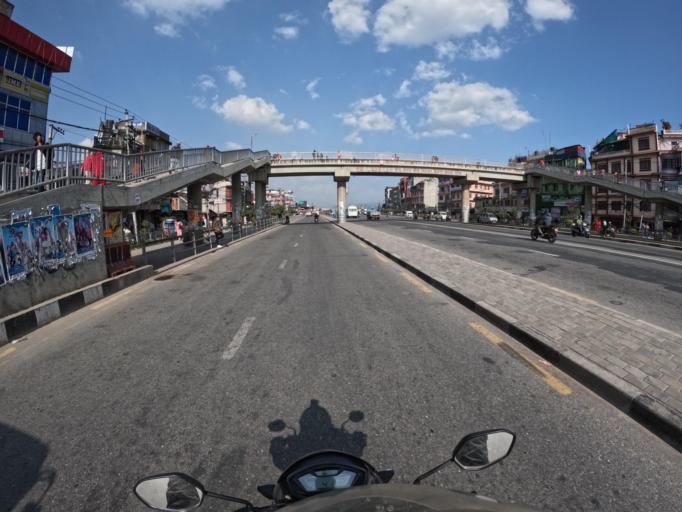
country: NP
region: Central Region
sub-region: Bagmati Zone
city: Patan
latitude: 27.6777
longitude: 85.3474
